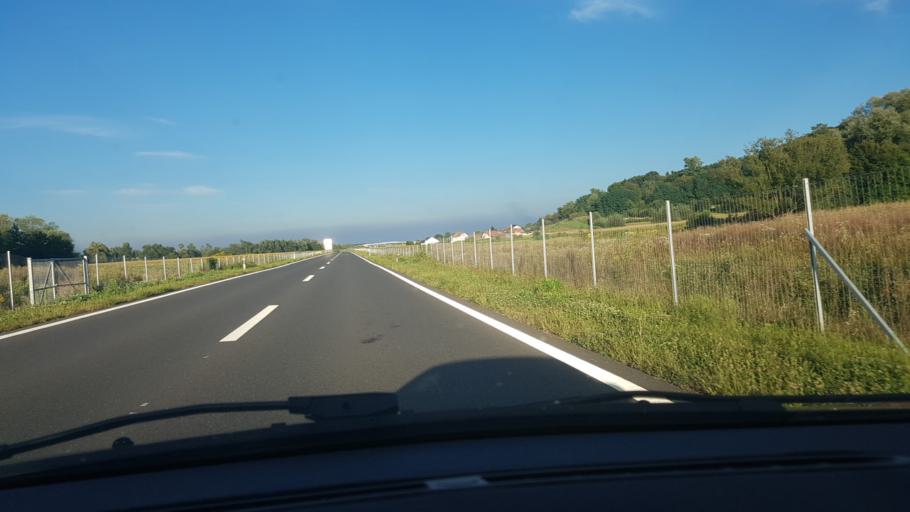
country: HR
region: Krapinsko-Zagorska
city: Selnica
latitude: 46.0377
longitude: 16.0351
